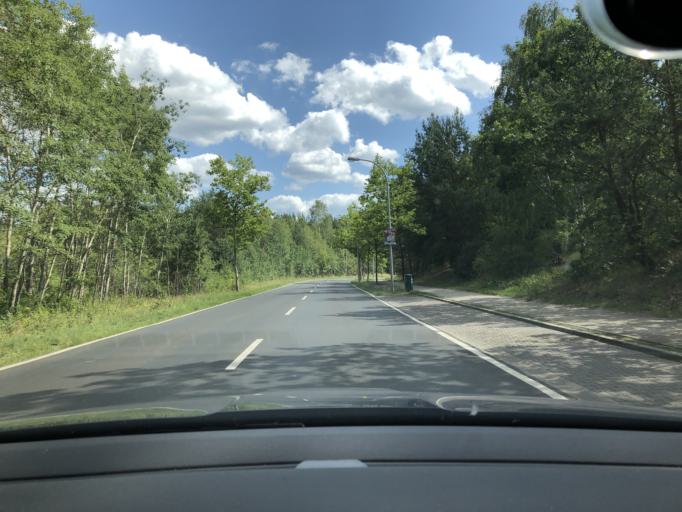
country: DE
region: Brandenburg
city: Oranienburg
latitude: 52.7714
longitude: 13.2663
